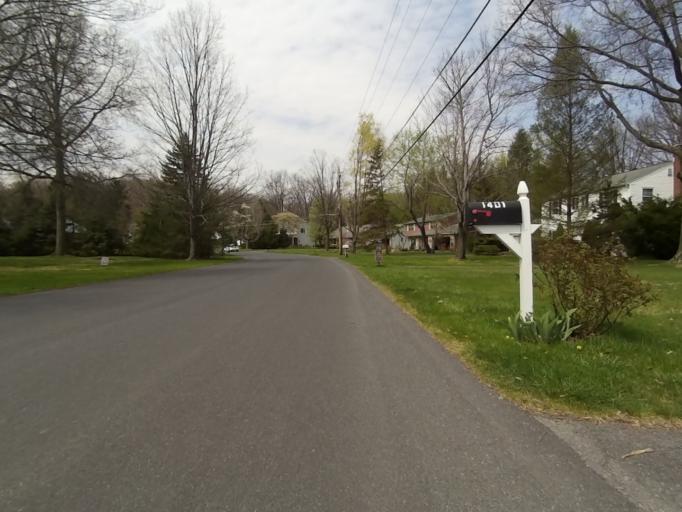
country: US
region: Pennsylvania
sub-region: Centre County
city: Park Forest Village
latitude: 40.7988
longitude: -77.8979
